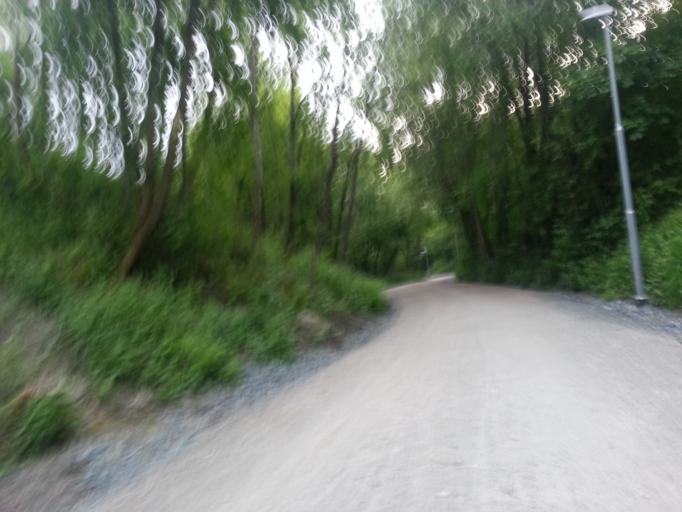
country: NO
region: Sor-Trondelag
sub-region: Trondheim
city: Trondheim
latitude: 63.4141
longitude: 10.4250
